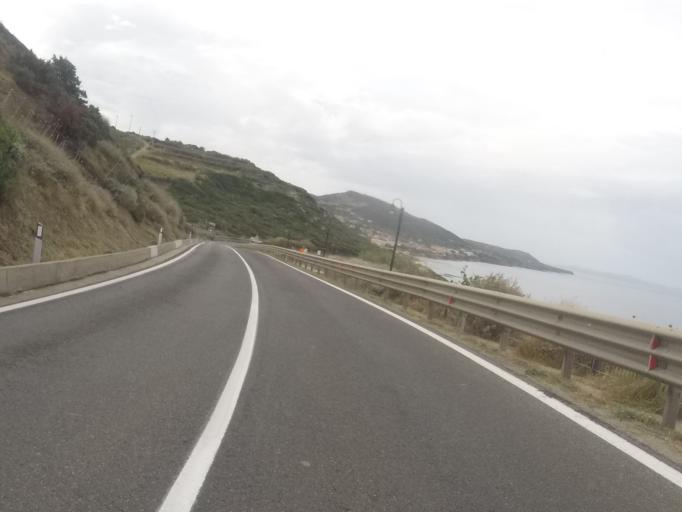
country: IT
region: Sardinia
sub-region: Provincia di Sassari
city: Lu Bagnu
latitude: 40.9115
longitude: 8.6951
